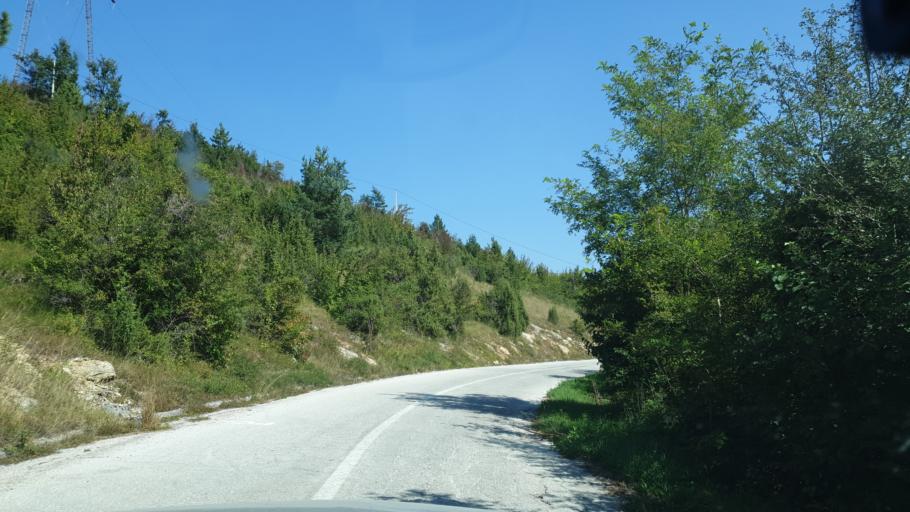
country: RS
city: Zlatibor
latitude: 43.6537
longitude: 19.8263
